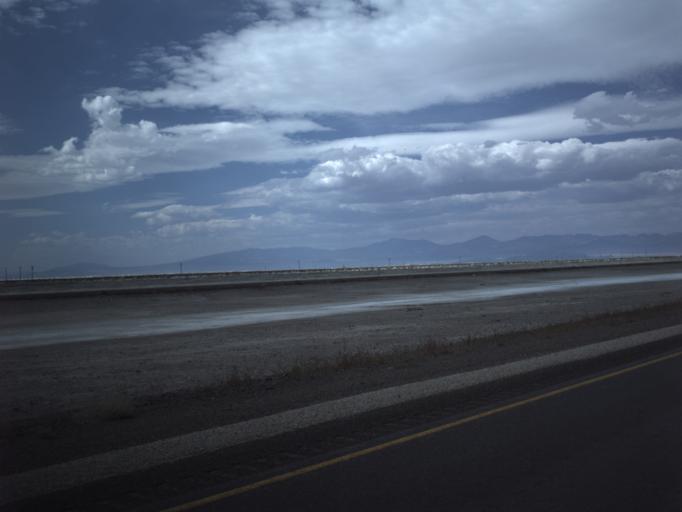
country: US
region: Utah
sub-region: Tooele County
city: Wendover
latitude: 40.7384
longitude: -113.8027
